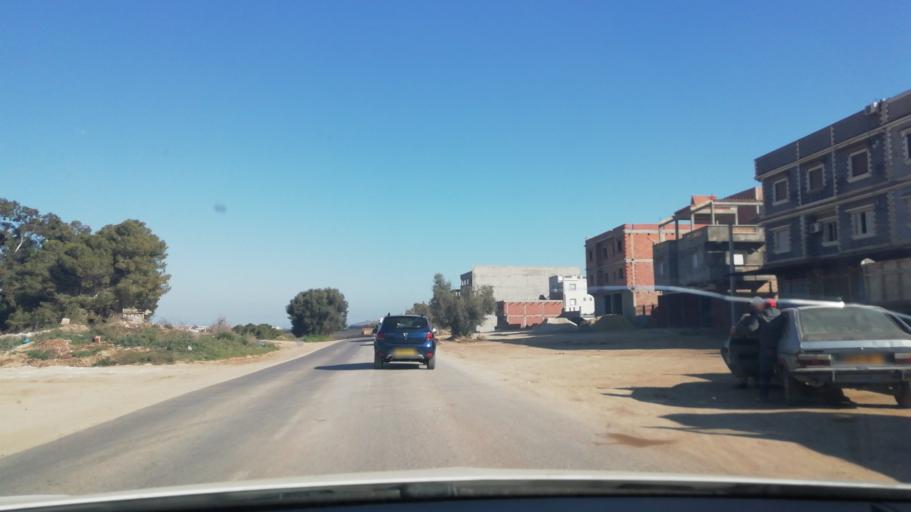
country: DZ
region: Tlemcen
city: Nedroma
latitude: 35.0189
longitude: -1.8940
